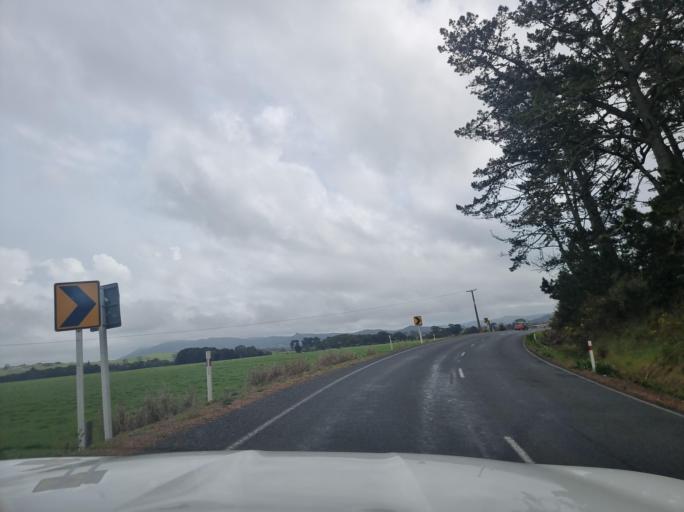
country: NZ
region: Northland
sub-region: Whangarei
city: Ruakaka
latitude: -35.9938
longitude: 174.4633
